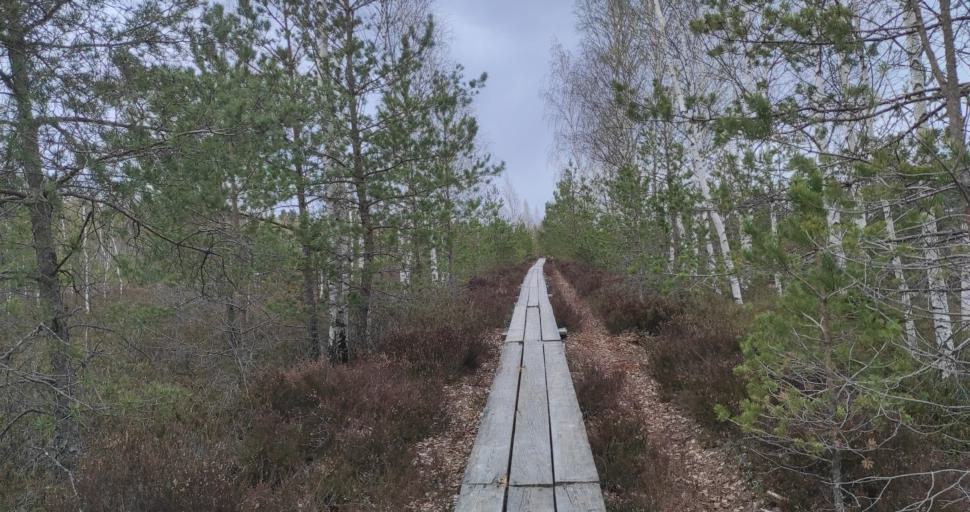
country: LV
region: Dundaga
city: Dundaga
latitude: 57.3542
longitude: 22.1523
